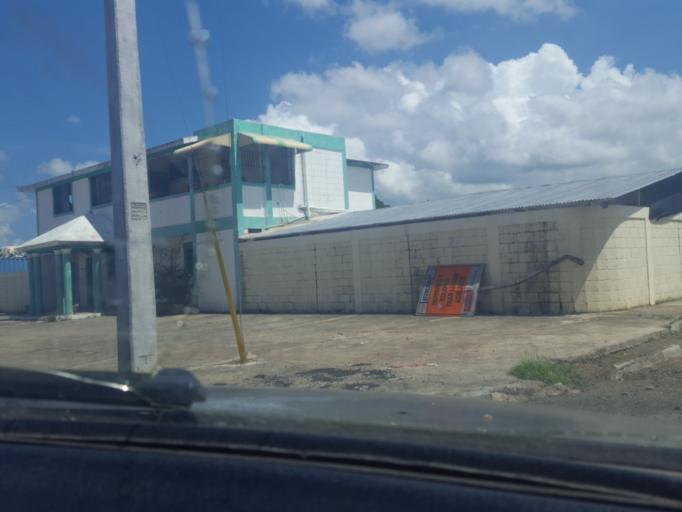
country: DO
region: Santiago
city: Santiago de los Caballeros
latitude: 19.4952
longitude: -70.6965
